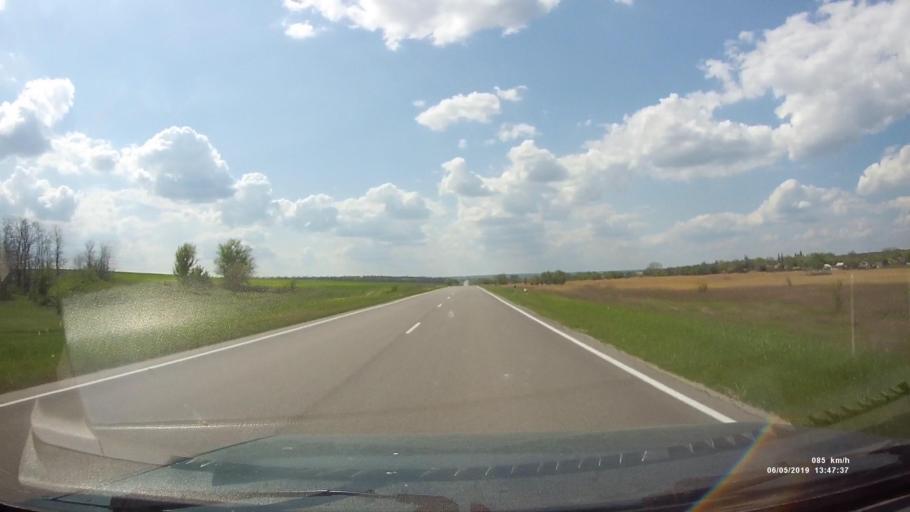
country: RU
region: Rostov
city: Melikhovskaya
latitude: 47.6574
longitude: 40.5593
